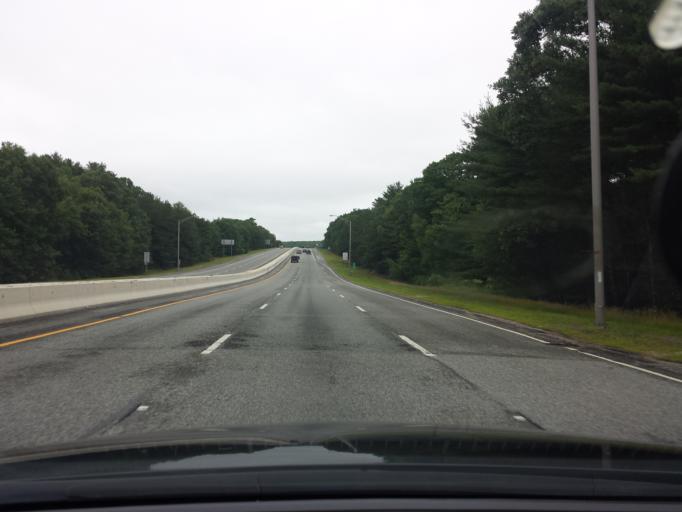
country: US
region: Rhode Island
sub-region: Washington County
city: Hope Valley
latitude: 41.5154
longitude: -71.6903
